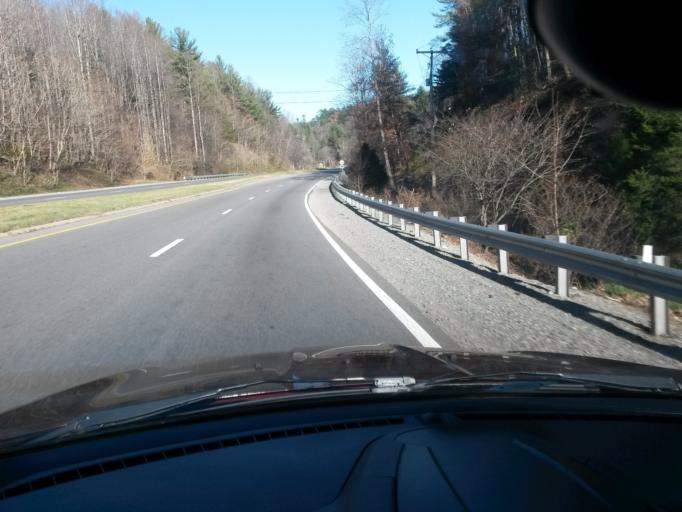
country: US
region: Virginia
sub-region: Roanoke County
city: Narrows
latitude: 37.1647
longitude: -79.9451
